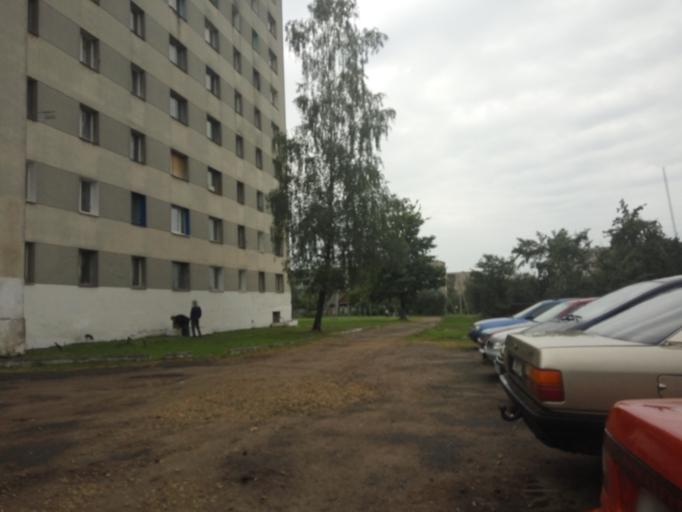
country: BY
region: Vitebsk
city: Vitebsk
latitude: 55.2015
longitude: 30.2498
